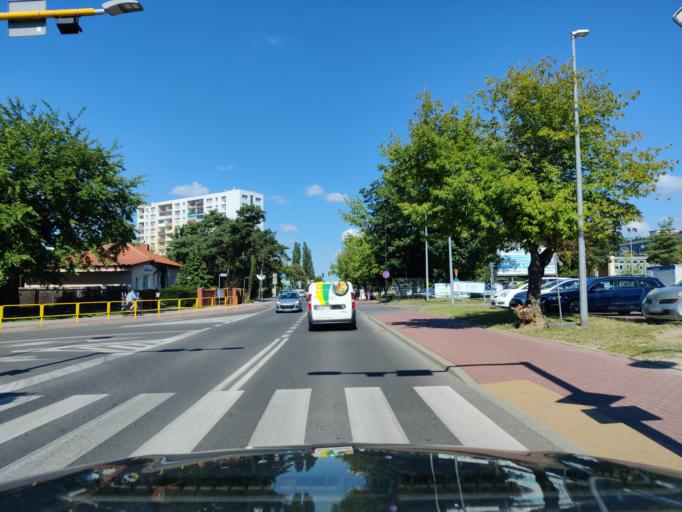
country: PL
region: Masovian Voivodeship
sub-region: Powiat legionowski
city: Legionowo
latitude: 52.3932
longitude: 20.9339
